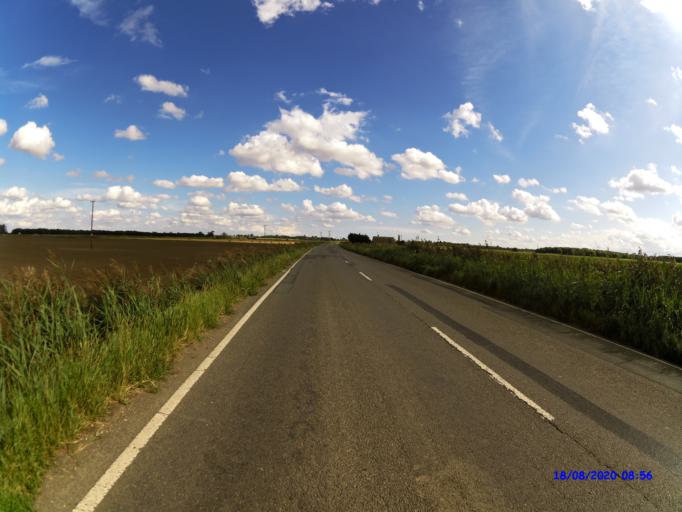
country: GB
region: England
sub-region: Cambridgeshire
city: Ramsey
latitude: 52.4795
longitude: -0.1015
